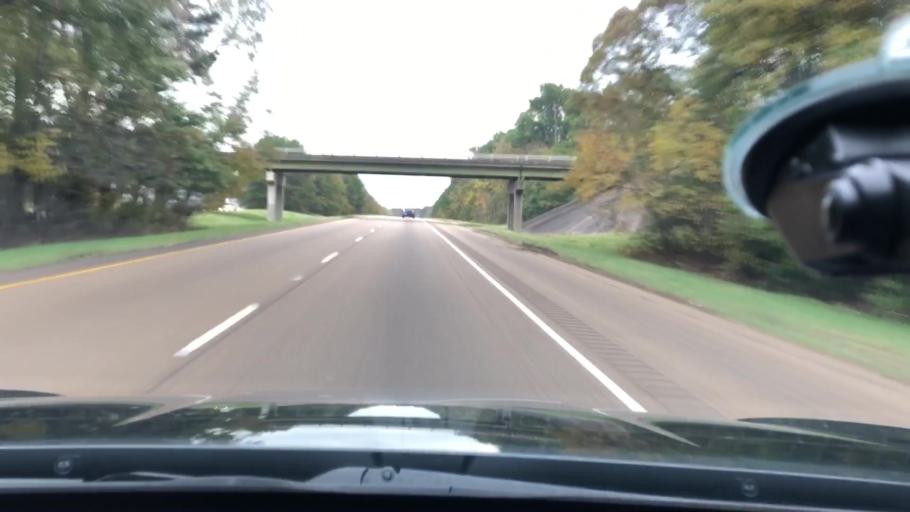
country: US
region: Arkansas
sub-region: Nevada County
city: Prescott
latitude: 33.7763
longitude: -93.4699
